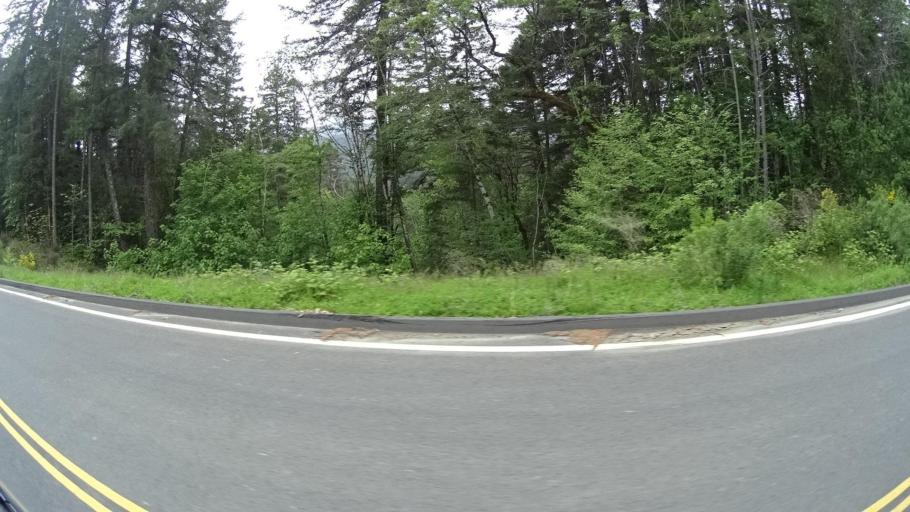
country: US
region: California
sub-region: Humboldt County
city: Willow Creek
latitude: 41.1225
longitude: -123.7427
